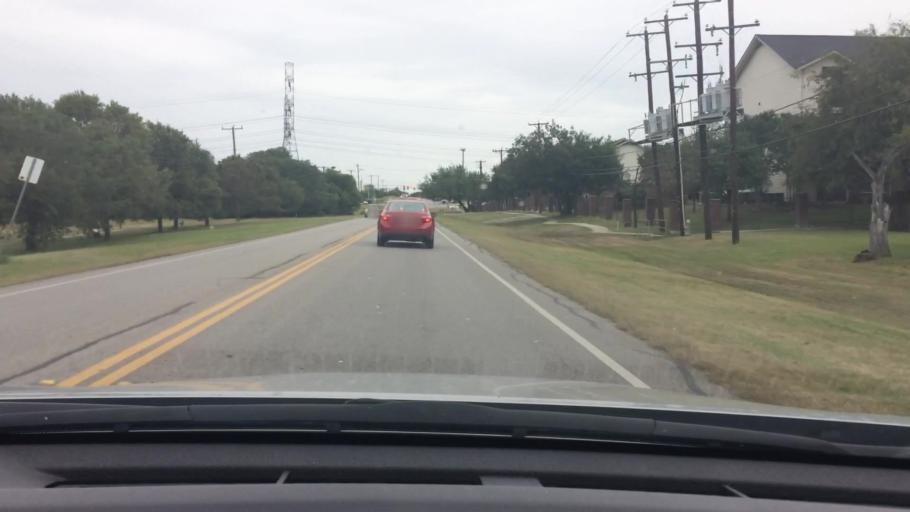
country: US
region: Texas
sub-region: Bexar County
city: Windcrest
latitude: 29.5409
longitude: -98.3693
